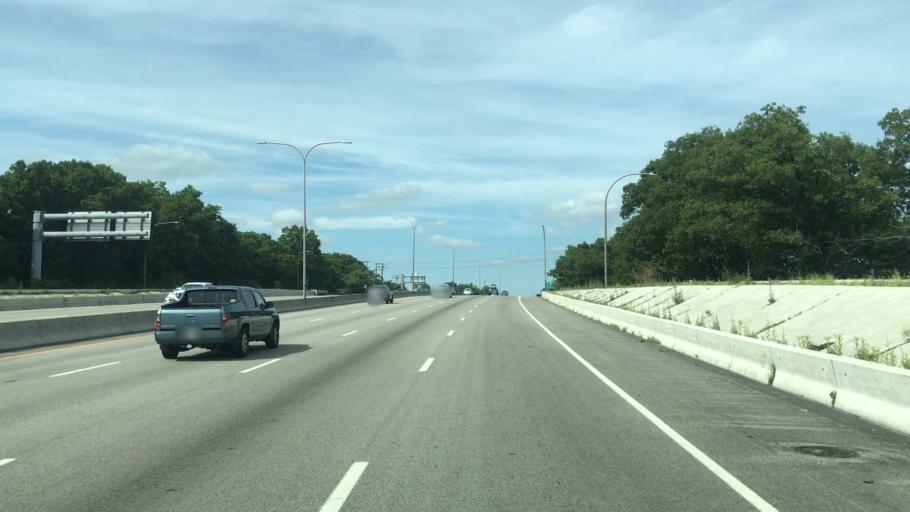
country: US
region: Rhode Island
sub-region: Providence County
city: Cranston
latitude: 41.7834
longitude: -71.4234
